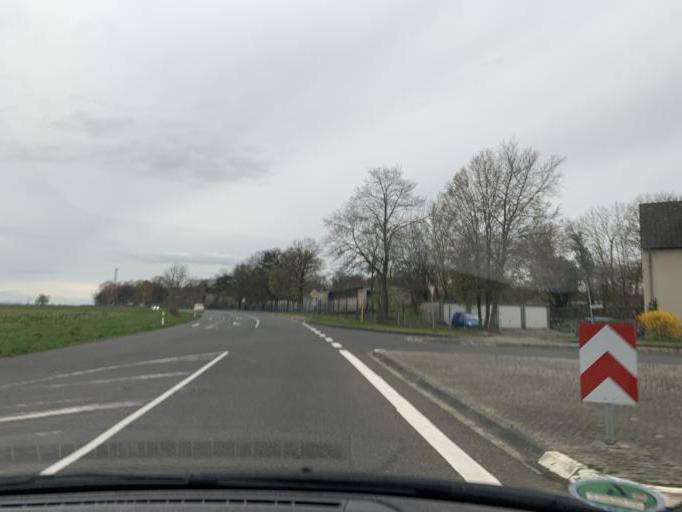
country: DE
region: North Rhine-Westphalia
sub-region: Regierungsbezirk Koln
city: Norvenich
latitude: 50.8053
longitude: 6.6525
